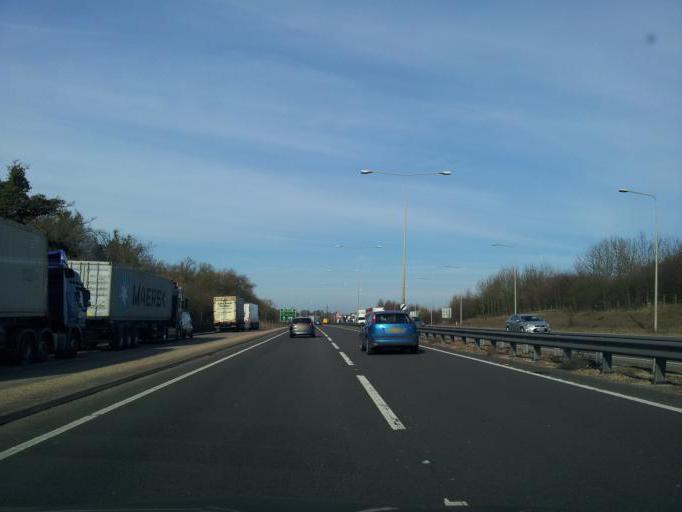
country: GB
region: England
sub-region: Cambridgeshire
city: Brampton
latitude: 52.3352
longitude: -0.2149
